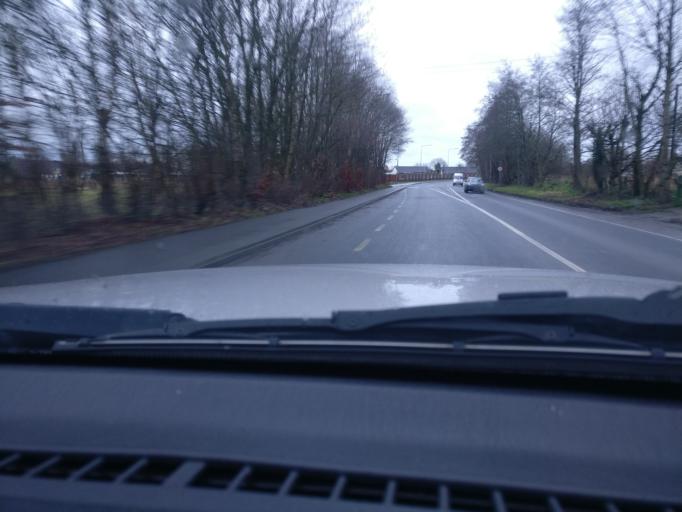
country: IE
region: Leinster
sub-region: An Mhi
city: Trim
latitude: 53.5506
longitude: -6.7872
